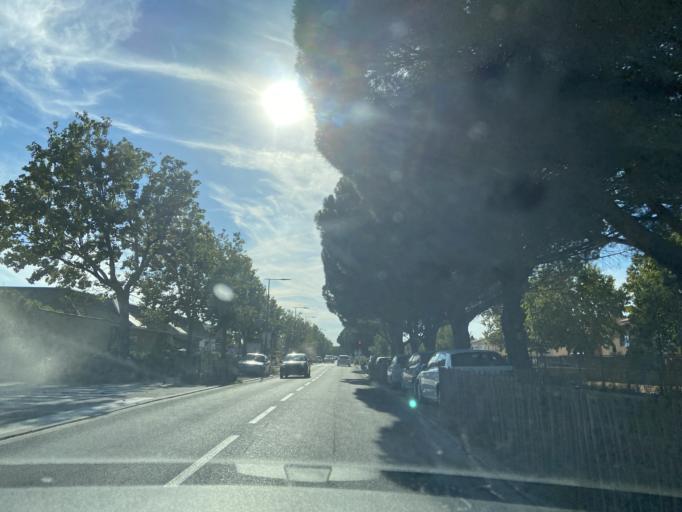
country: FR
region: Provence-Alpes-Cote d'Azur
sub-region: Departement des Bouches-du-Rhone
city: Miramas
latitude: 43.5878
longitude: 5.0007
